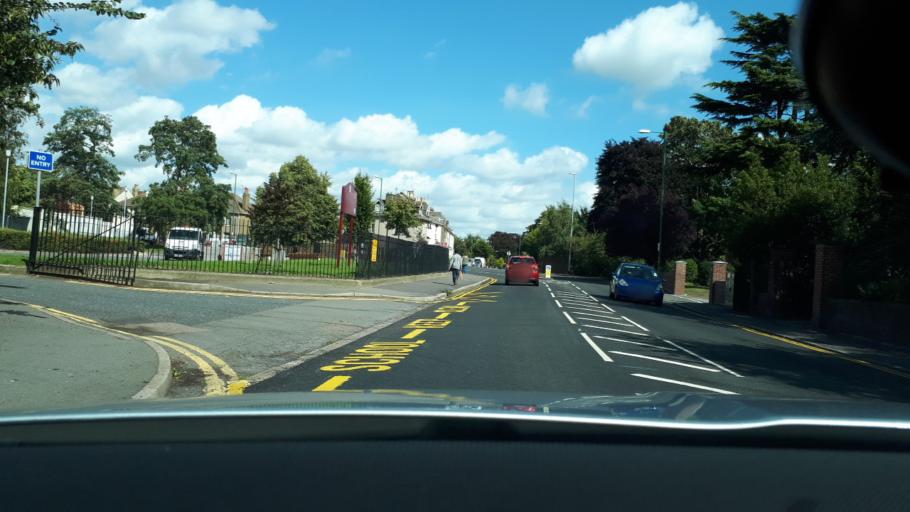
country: GB
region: England
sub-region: Kent
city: Dartford
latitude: 51.4439
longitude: 0.2047
